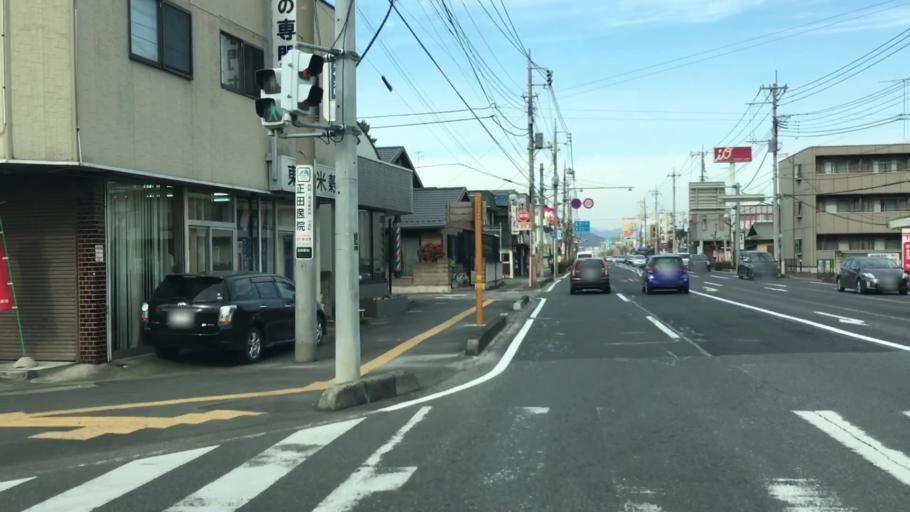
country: JP
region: Saitama
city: Menuma
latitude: 36.2602
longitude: 139.3768
